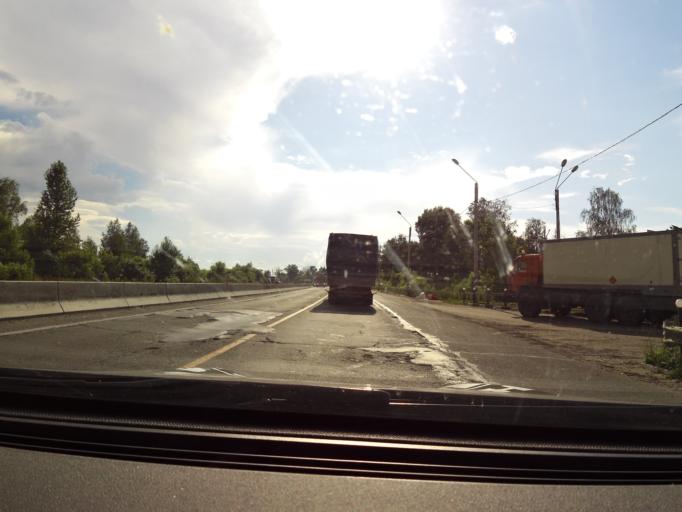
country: RU
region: Nizjnij Novgorod
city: Mulino
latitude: 56.2763
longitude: 42.9755
